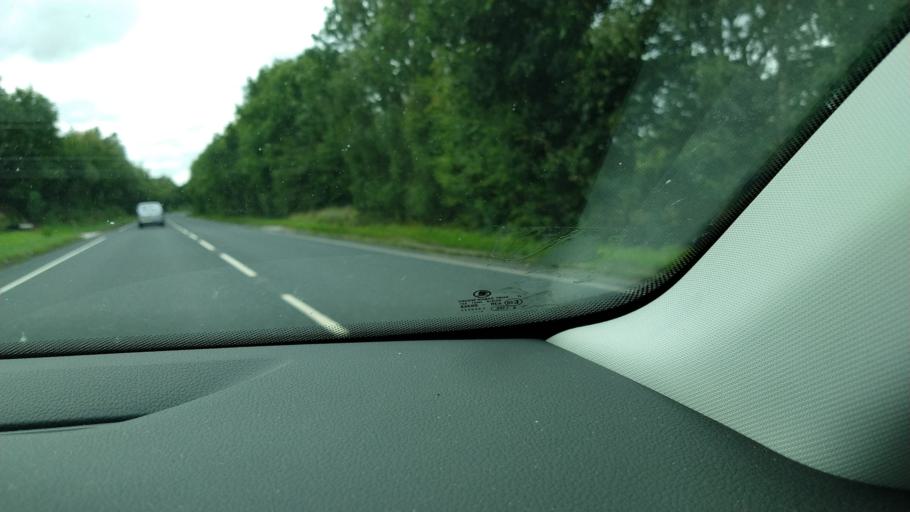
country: GB
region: England
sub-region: North Yorkshire
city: Camblesforth
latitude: 53.7240
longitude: -0.9853
